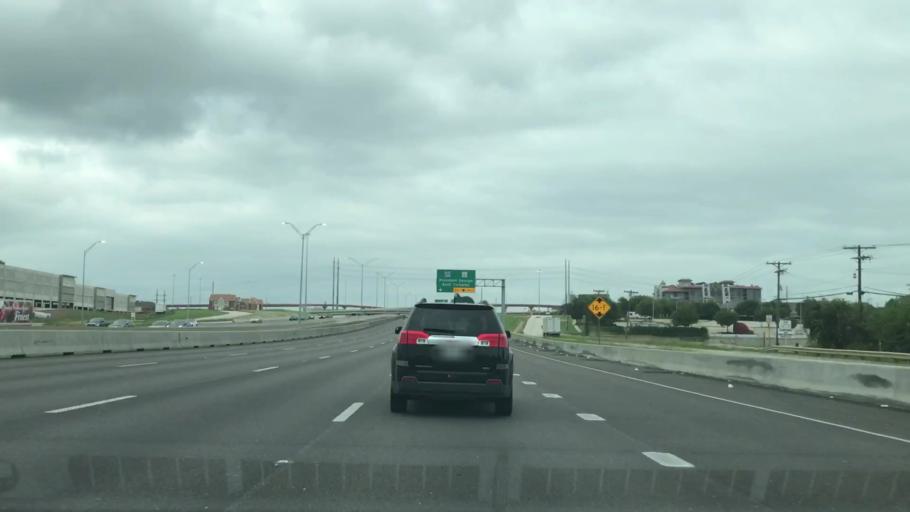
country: US
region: Texas
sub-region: Tarrant County
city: Euless
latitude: 32.8365
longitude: -97.0283
